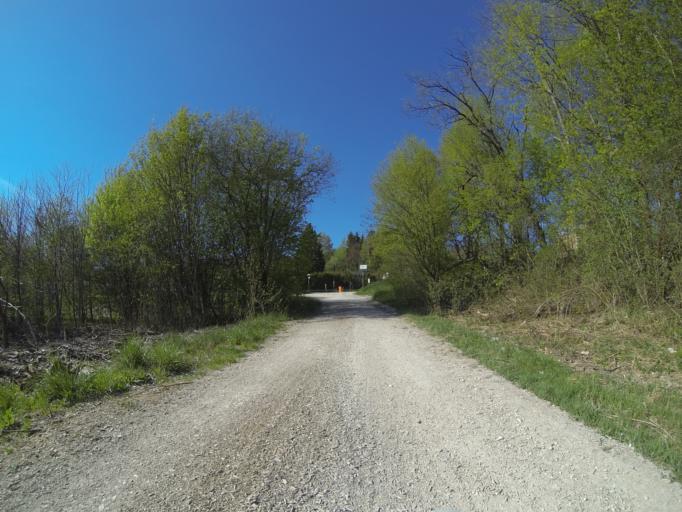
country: DE
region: Baden-Wuerttemberg
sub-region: Tuebingen Region
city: Ulm
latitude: 48.3750
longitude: 9.9582
